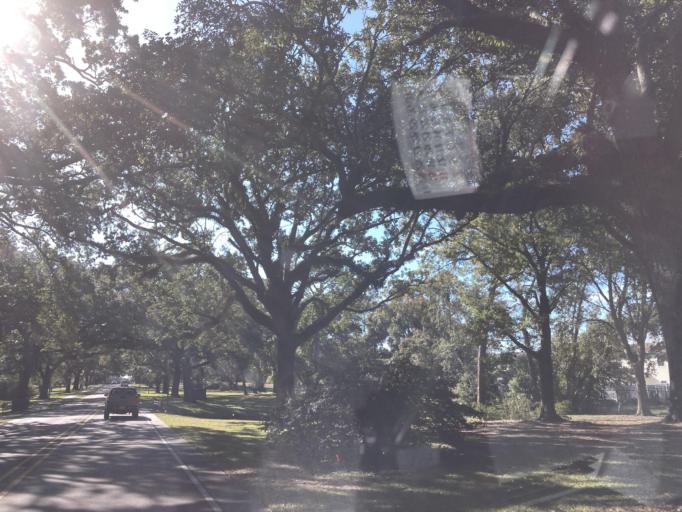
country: US
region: Mississippi
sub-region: Harrison County
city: D'Iberville
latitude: 30.4073
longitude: -88.9472
